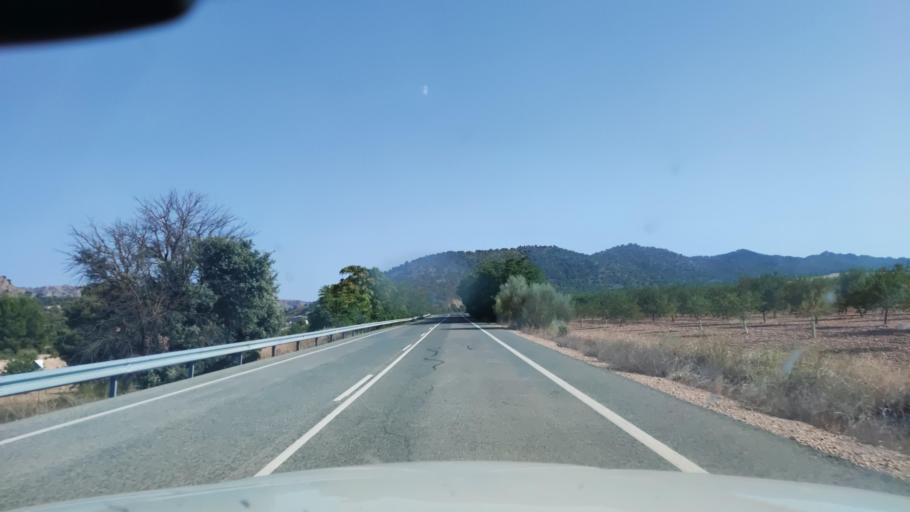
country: ES
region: Castille-La Mancha
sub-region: Provincia de Albacete
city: Tobarra
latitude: 38.6807
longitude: -1.6722
